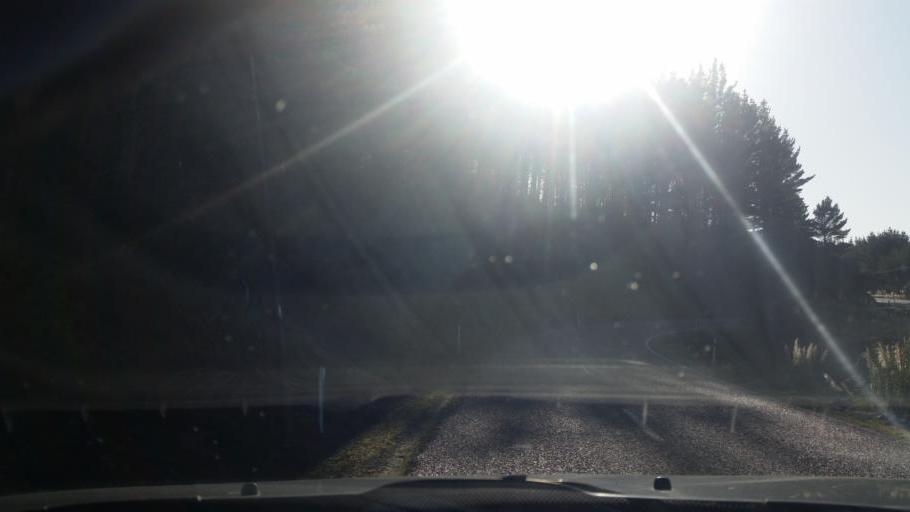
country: NZ
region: Auckland
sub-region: Auckland
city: Wellsford
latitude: -36.2174
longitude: 174.4657
